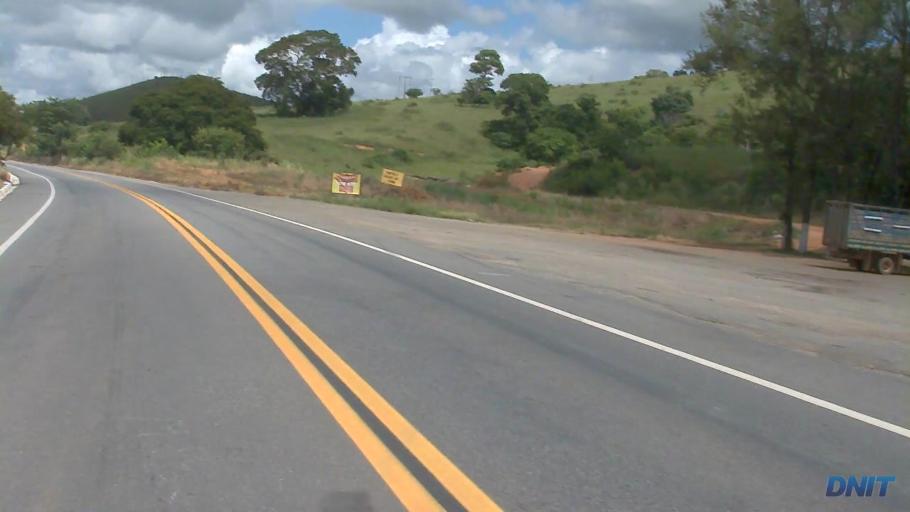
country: BR
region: Minas Gerais
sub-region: Governador Valadares
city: Governador Valadares
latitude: -18.9352
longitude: -42.0512
